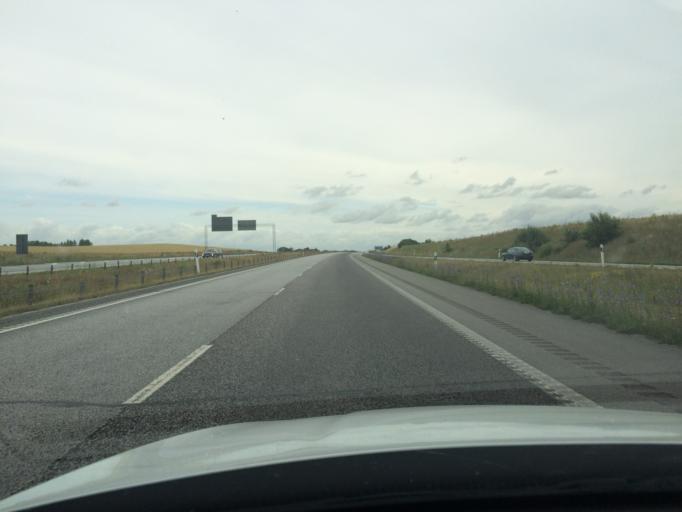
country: SE
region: Skane
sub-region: Malmo
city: Oxie
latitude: 55.5628
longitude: 13.0820
